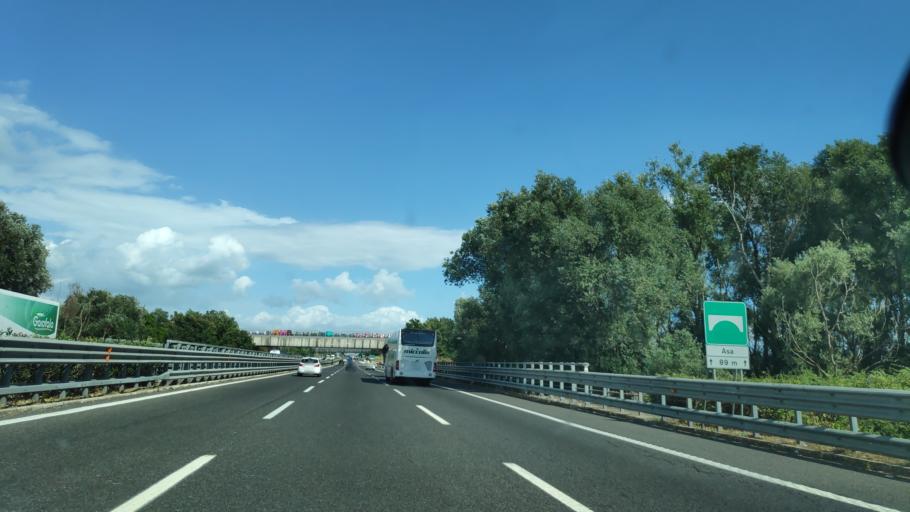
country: IT
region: Campania
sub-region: Provincia di Salerno
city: Pagliarone
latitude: 40.6356
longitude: 14.9124
